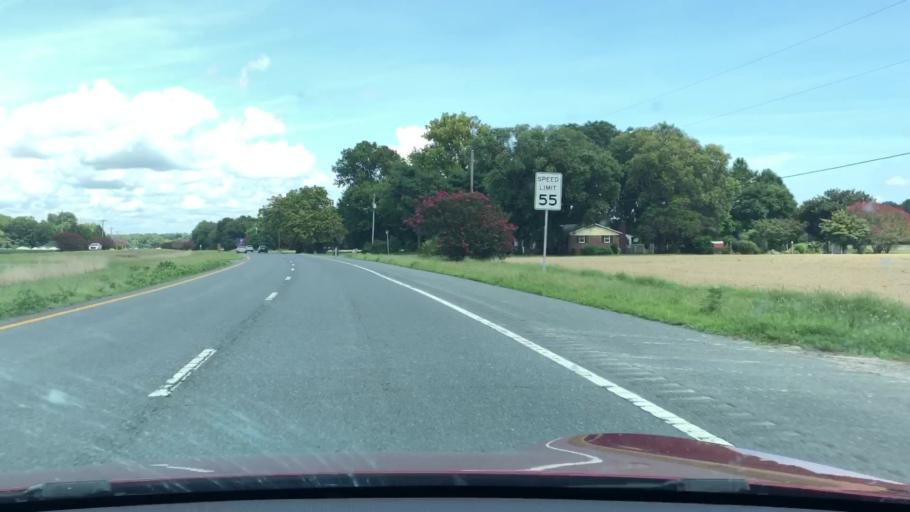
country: US
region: Virginia
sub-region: Northampton County
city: Cape Charles
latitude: 37.2961
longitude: -75.9707
